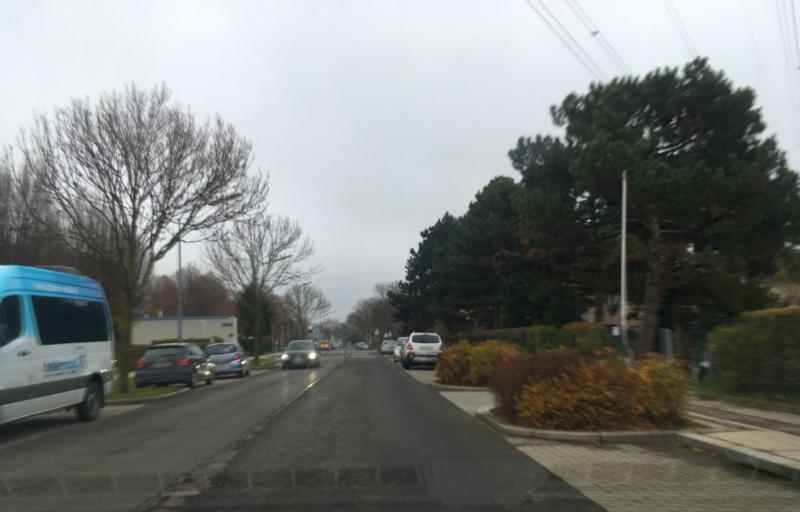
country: AT
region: Lower Austria
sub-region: Politischer Bezirk Wien-Umgebung
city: Gerasdorf bei Wien
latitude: 48.2147
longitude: 16.4700
